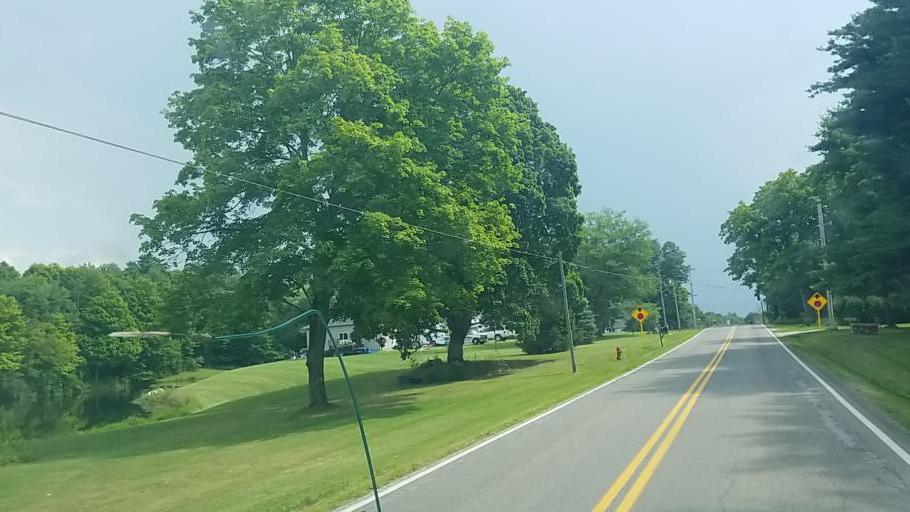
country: US
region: Ohio
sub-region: Medina County
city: Lodi
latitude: 41.0486
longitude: -82.0055
